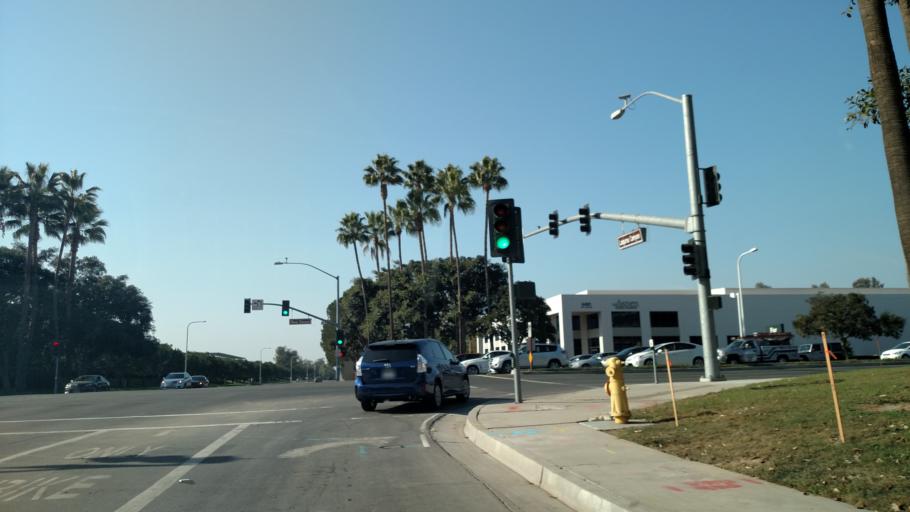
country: US
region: California
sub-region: Orange County
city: Irvine
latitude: 33.6732
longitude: -117.7621
